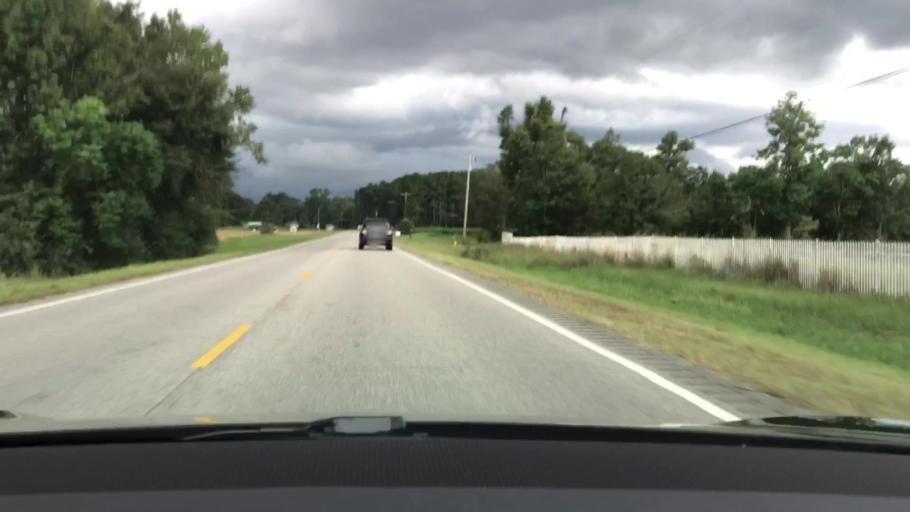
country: US
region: Alabama
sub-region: Coffee County
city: Elba
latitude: 31.4808
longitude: -86.0576
